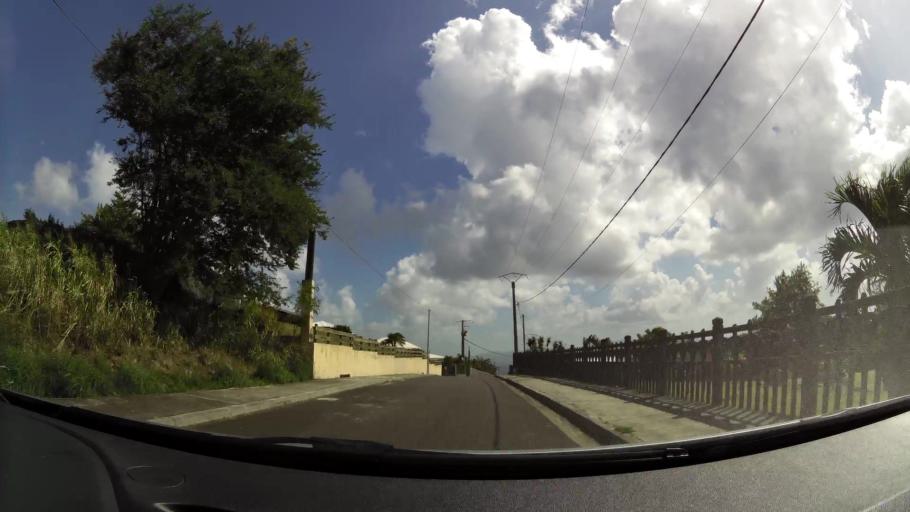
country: MQ
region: Martinique
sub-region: Martinique
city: Fort-de-France
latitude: 14.6331
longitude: -61.1236
